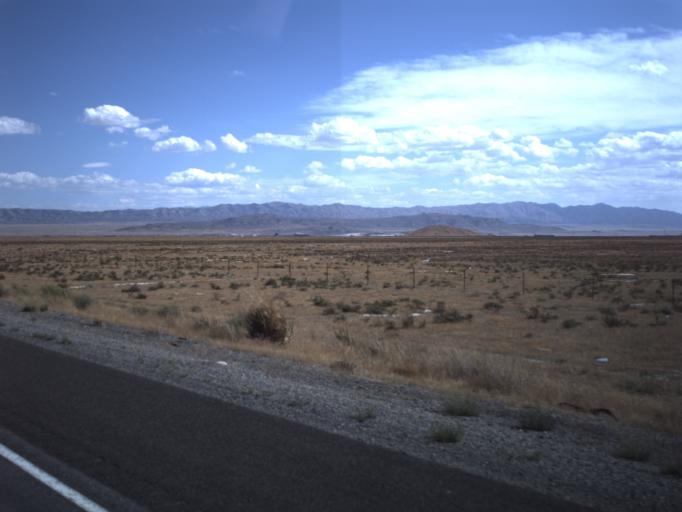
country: US
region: Utah
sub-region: Tooele County
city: Grantsville
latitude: 40.7255
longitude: -113.1755
